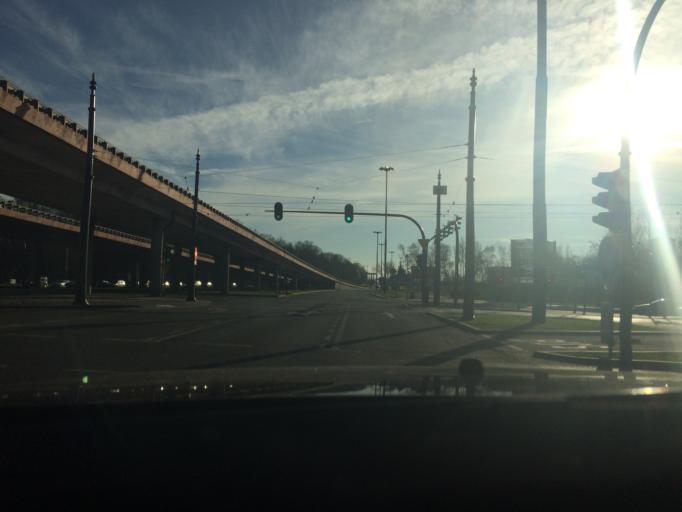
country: PL
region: Lodz Voivodeship
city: Lodz
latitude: 51.7564
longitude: 19.4344
